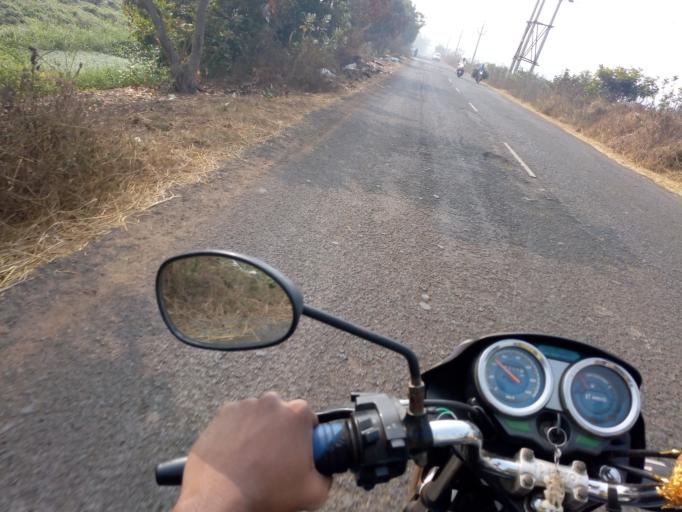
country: IN
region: Andhra Pradesh
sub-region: West Godavari
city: Tadepallegudem
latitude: 16.7729
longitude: 81.4254
